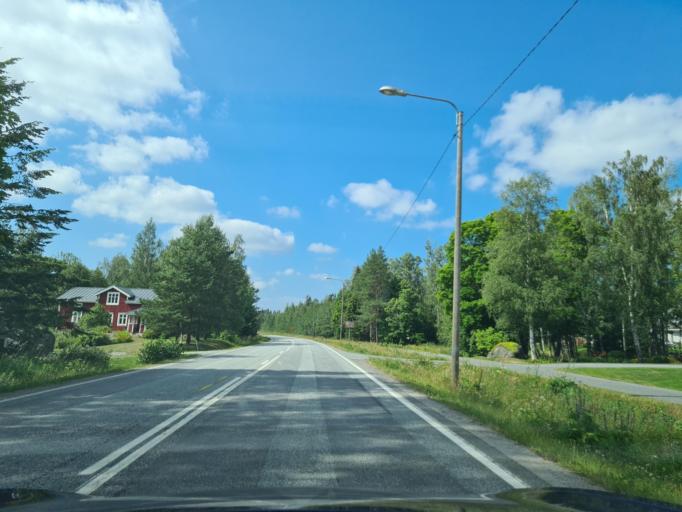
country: FI
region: Ostrobothnia
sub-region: Vaasa
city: Vaasa
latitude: 63.1941
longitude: 21.5547
